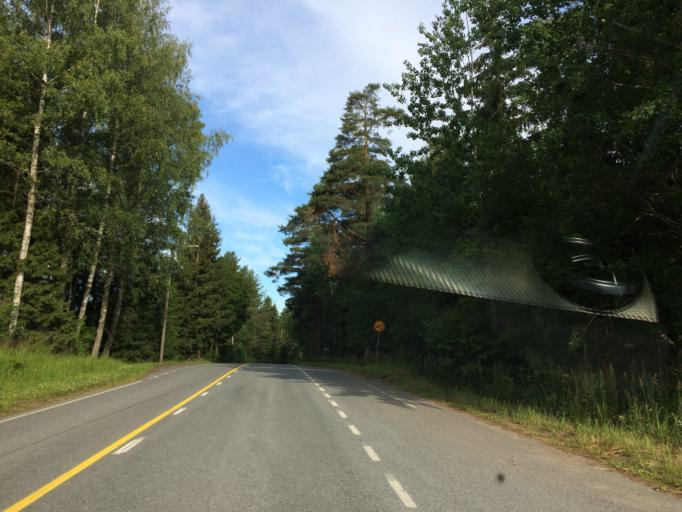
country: FI
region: Haeme
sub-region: Haemeenlinna
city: Janakkala
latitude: 60.9289
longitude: 24.5771
